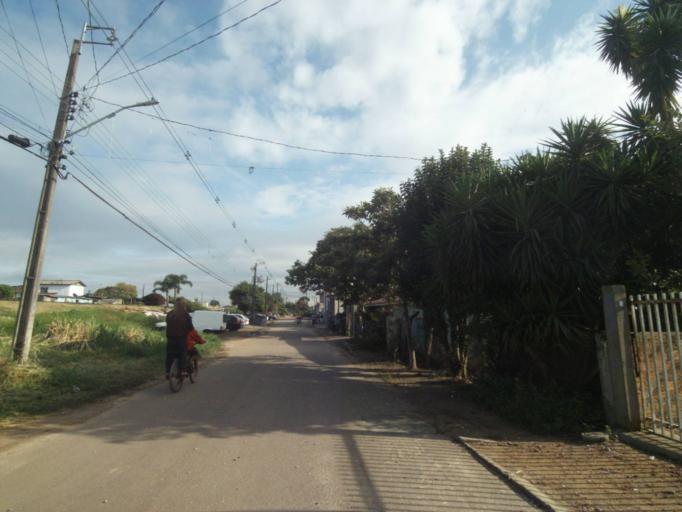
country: BR
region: Parana
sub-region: Pinhais
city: Pinhais
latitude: -25.4611
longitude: -49.1988
